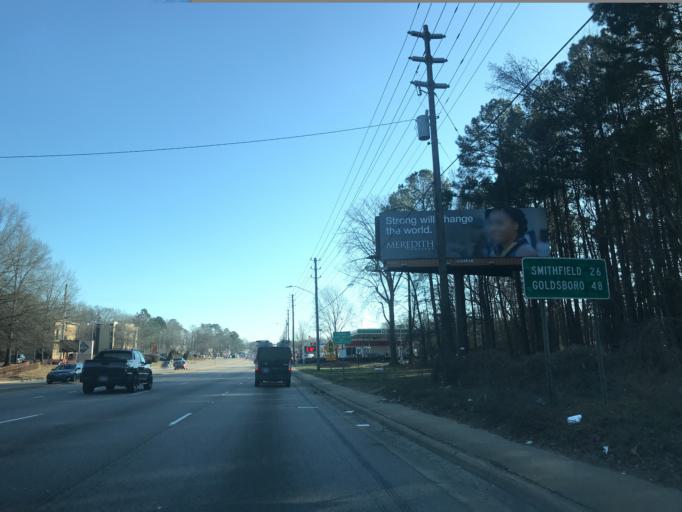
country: US
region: North Carolina
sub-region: Wake County
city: Raleigh
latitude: 35.7512
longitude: -78.6491
